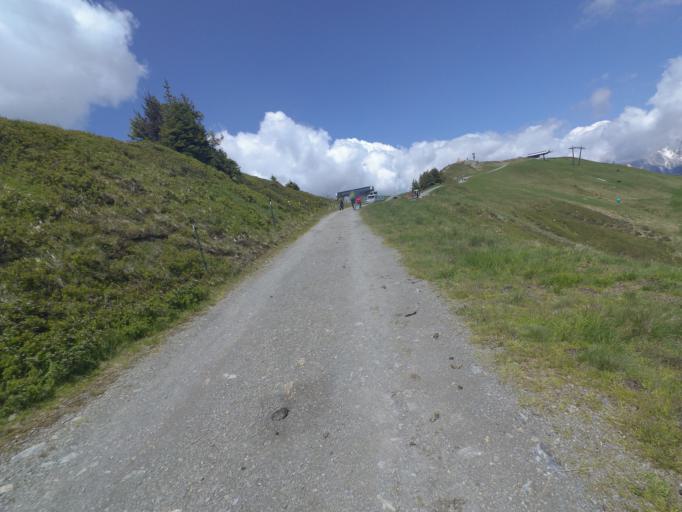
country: AT
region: Salzburg
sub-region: Politischer Bezirk Zell am See
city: Viehhofen
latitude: 47.3990
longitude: 12.7035
